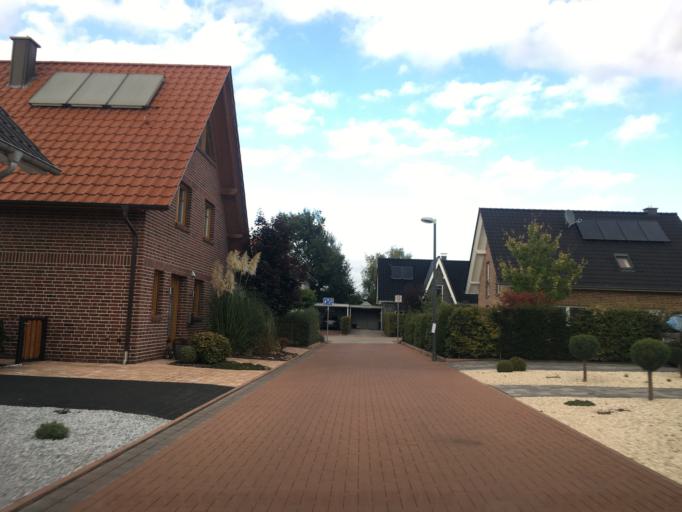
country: DE
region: North Rhine-Westphalia
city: Olfen
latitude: 51.7645
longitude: 7.3852
